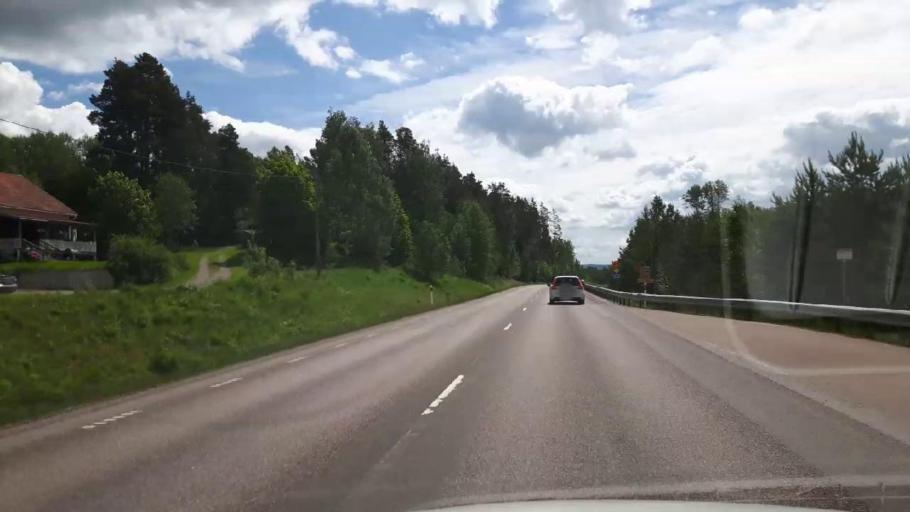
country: SE
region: Dalarna
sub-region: Saters Kommun
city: Saeter
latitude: 60.4569
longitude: 15.8046
